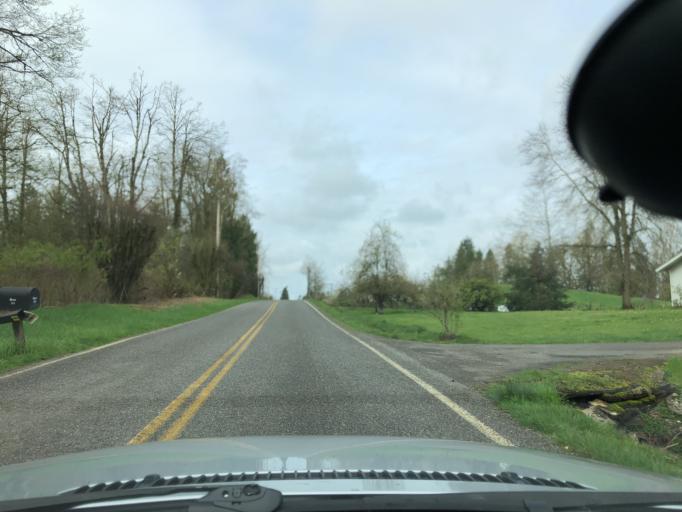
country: US
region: Washington
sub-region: Whatcom County
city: Lynden
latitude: 48.9831
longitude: -122.5320
